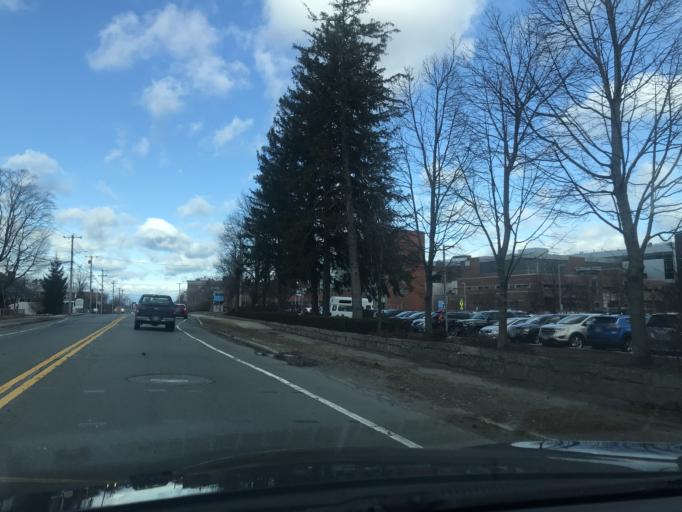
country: US
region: Massachusetts
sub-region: Norfolk County
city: Weymouth
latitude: 42.1739
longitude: -70.9554
